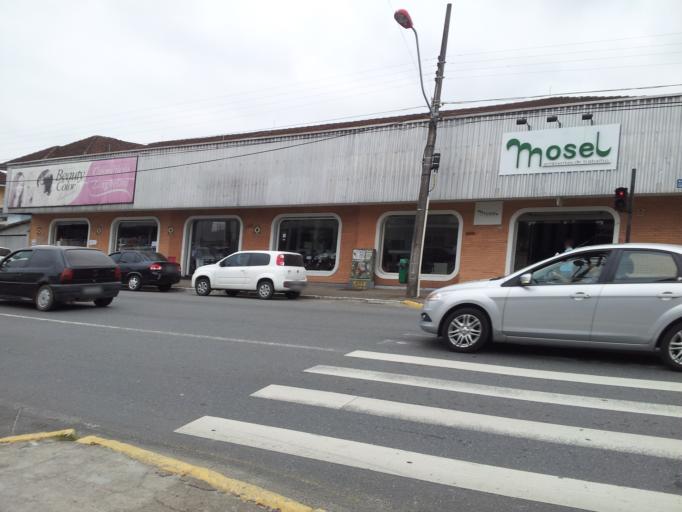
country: BR
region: Santa Catarina
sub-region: Joinville
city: Joinville
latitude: -26.3166
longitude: -48.8452
